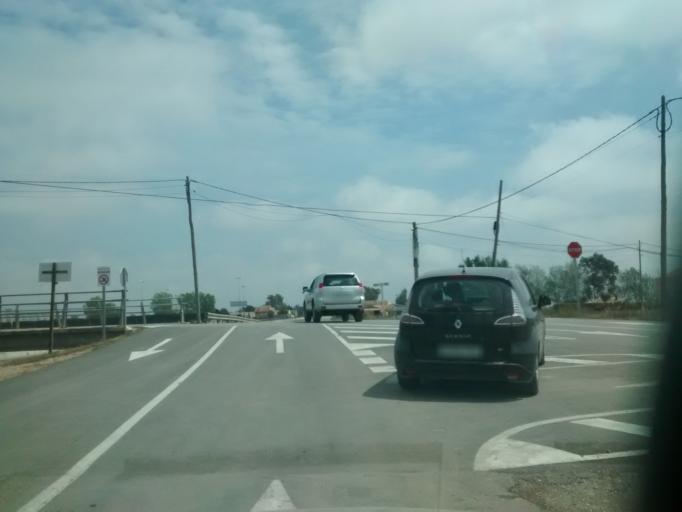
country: ES
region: Catalonia
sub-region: Provincia de Tarragona
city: Deltebre
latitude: 40.7022
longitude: 0.7300
